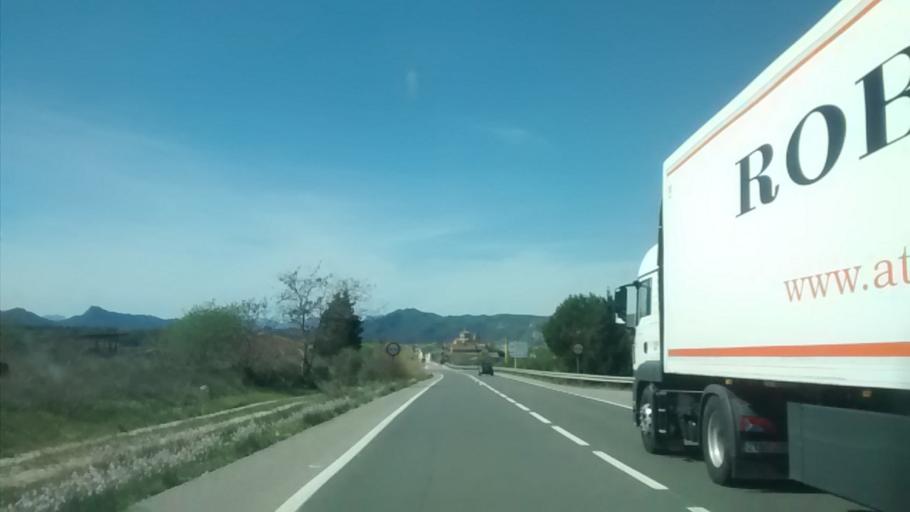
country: ES
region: Catalonia
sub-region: Provincia de Tarragona
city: Ginestar
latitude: 41.0454
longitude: 0.6440
